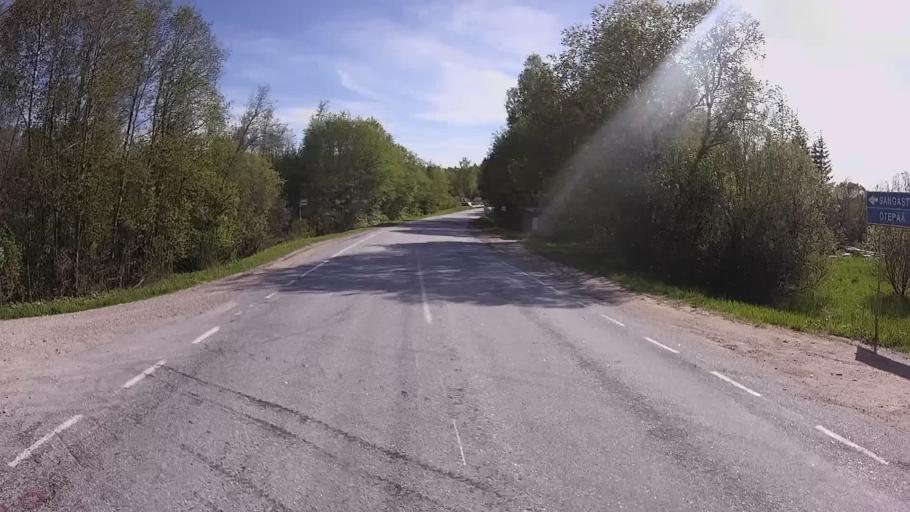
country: EE
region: Vorumaa
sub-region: Antsla vald
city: Vana-Antsla
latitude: 58.0217
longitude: 26.5034
